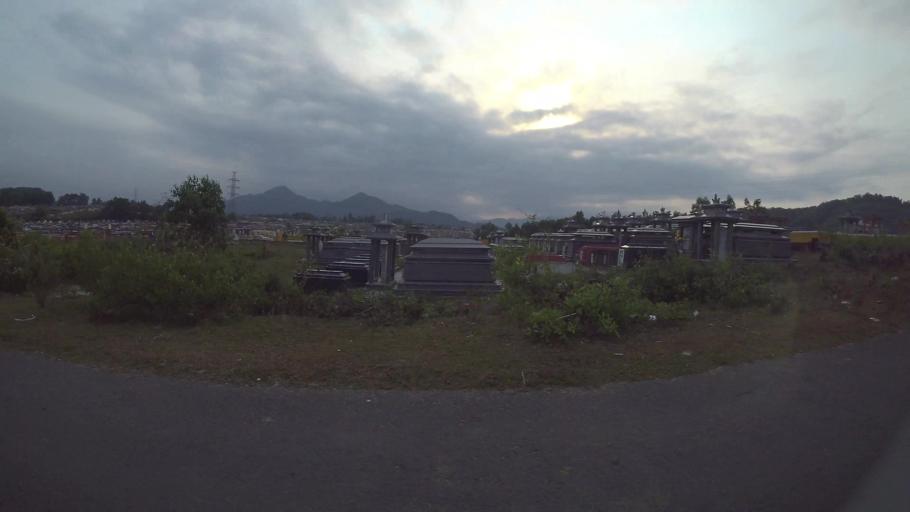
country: VN
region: Da Nang
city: Lien Chieu
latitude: 16.0613
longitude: 108.1118
